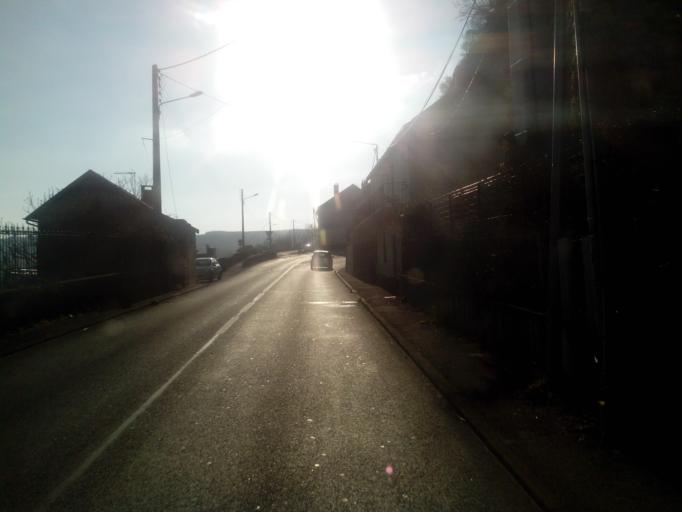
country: FR
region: Midi-Pyrenees
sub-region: Departement de l'Aveyron
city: Capdenac-Gare
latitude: 44.5760
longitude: 2.0706
